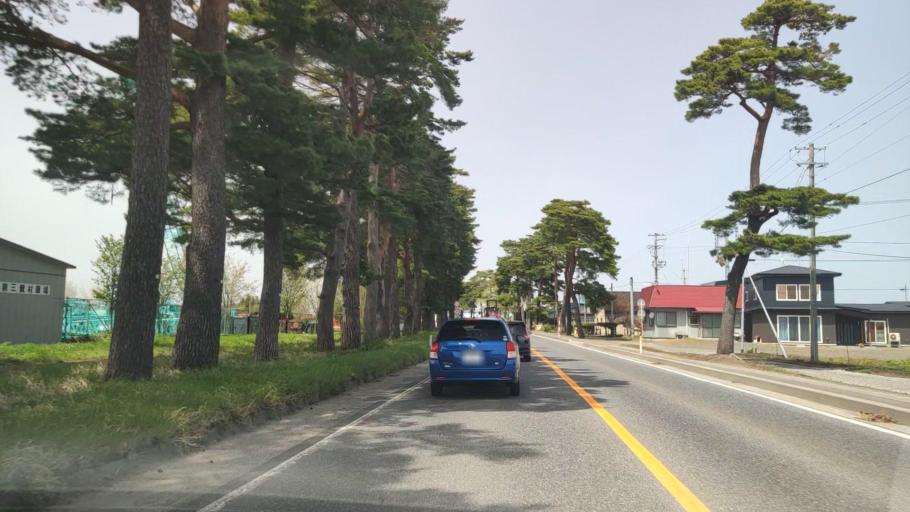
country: JP
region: Aomori
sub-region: Misawa Shi
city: Inuotose
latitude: 40.6701
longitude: 141.1840
